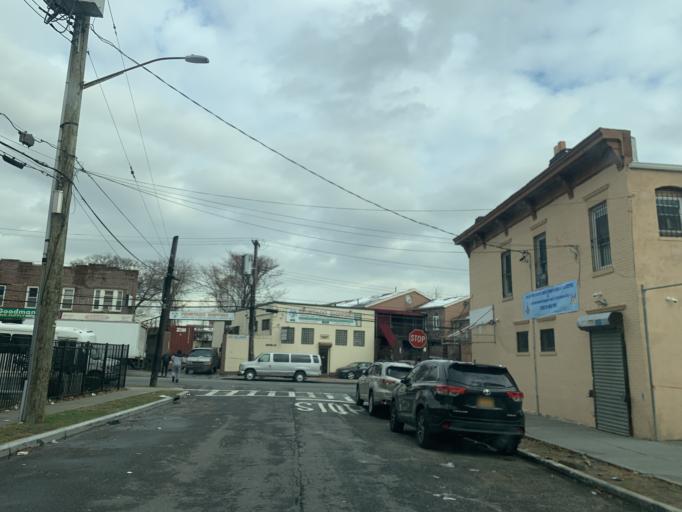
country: US
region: New York
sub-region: Queens County
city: Jamaica
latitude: 40.6897
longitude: -73.7868
